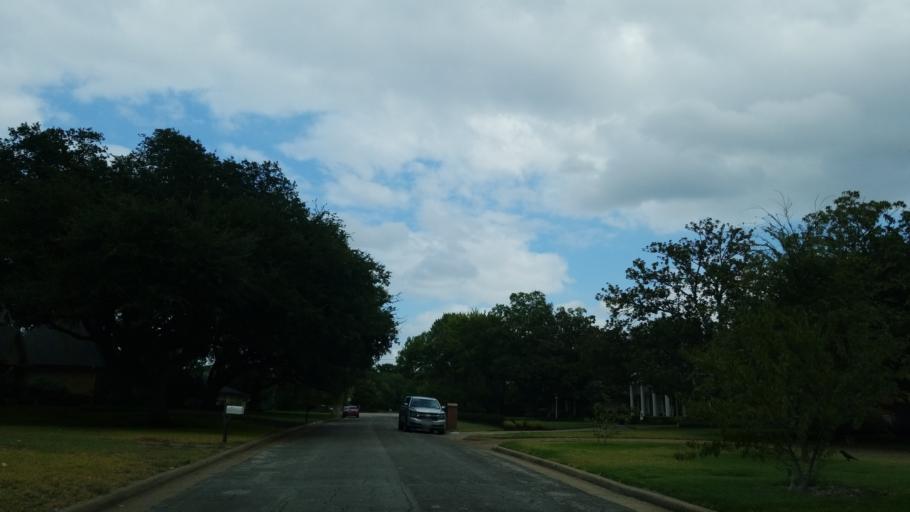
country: US
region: Texas
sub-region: Dallas County
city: Addison
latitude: 32.9467
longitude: -96.7871
